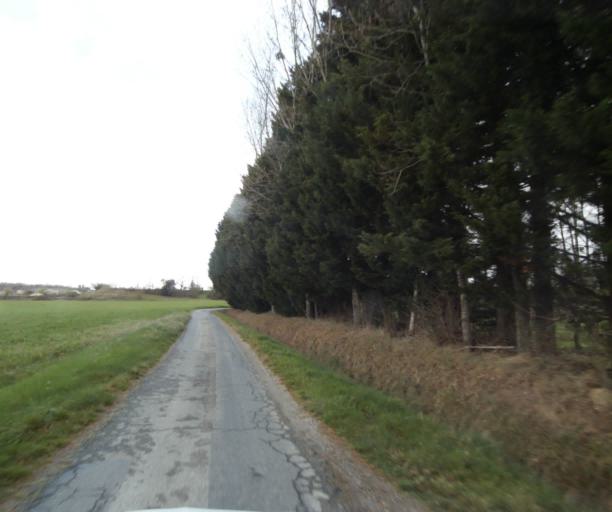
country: FR
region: Midi-Pyrenees
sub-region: Departement de l'Ariege
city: Saverdun
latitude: 43.2261
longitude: 1.5958
